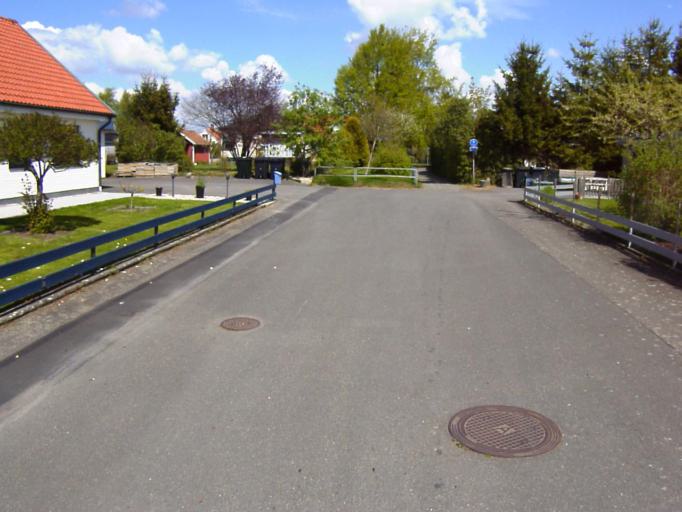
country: SE
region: Skane
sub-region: Kristianstads Kommun
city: Fjalkinge
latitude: 56.0147
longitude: 14.2301
